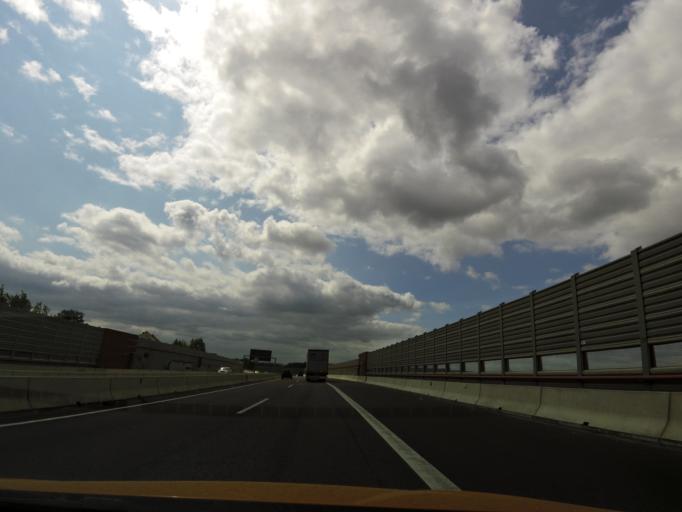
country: DE
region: Lower Saxony
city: Leiferde
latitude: 52.2275
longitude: 10.5026
